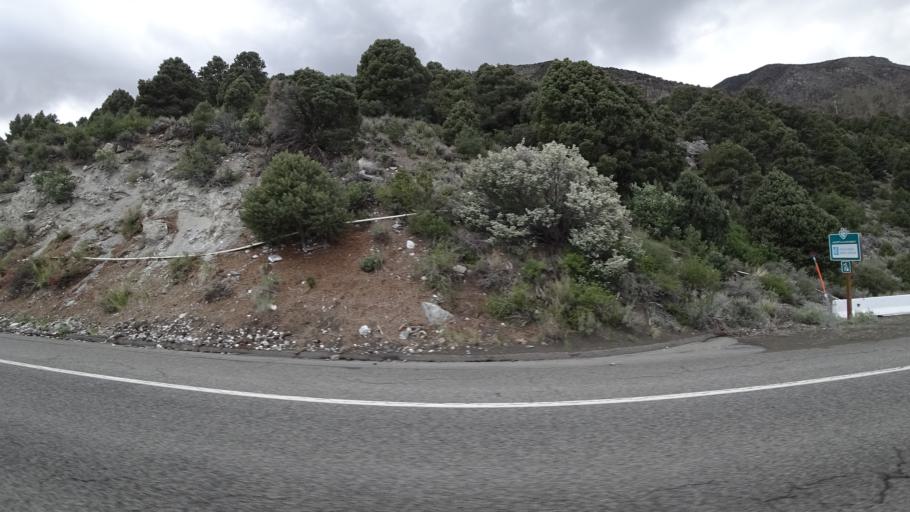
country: US
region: California
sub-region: Mono County
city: Bridgeport
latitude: 37.9692
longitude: -119.1314
